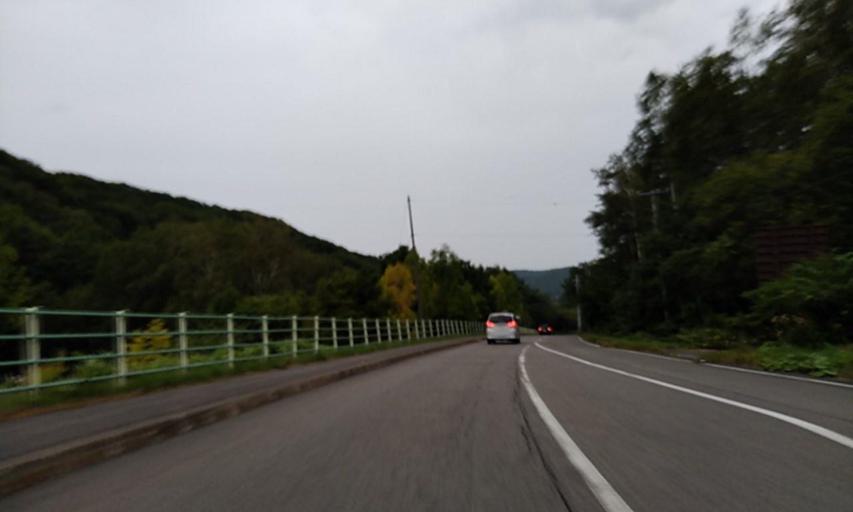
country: JP
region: Hokkaido
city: Abashiri
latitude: 43.9983
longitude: 144.2288
